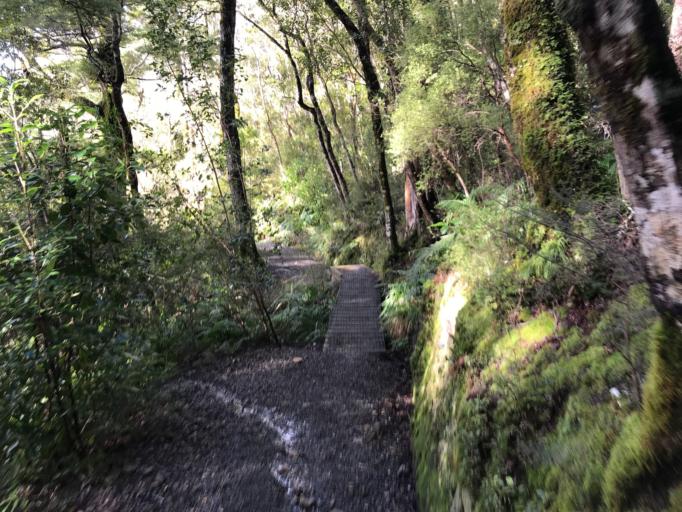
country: NZ
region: Wellington
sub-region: Masterton District
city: Masterton
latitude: -40.9039
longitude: 175.4554
